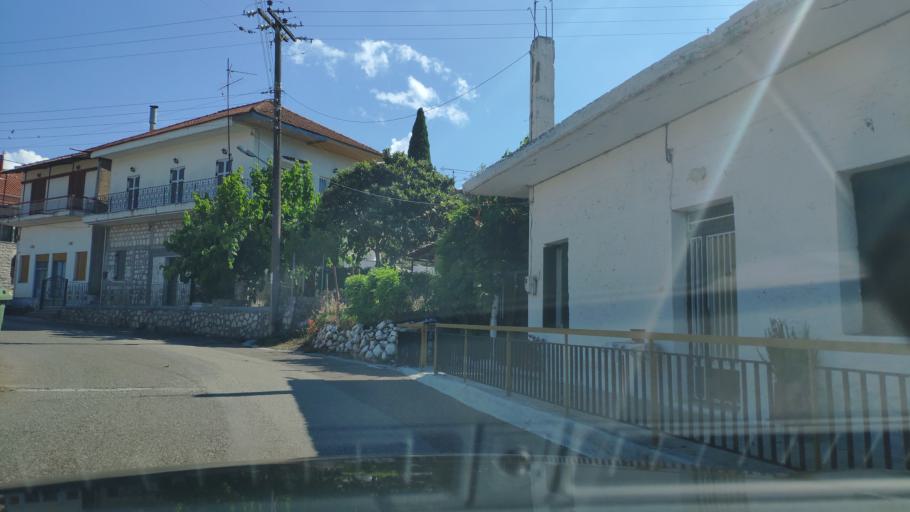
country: GR
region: West Greece
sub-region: Nomos Aitolias kai Akarnanias
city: Katouna
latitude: 38.7894
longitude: 21.1149
